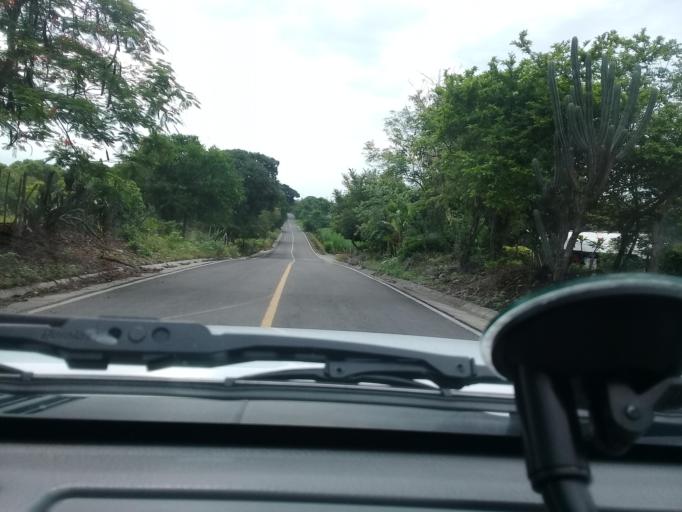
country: MX
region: Veracruz
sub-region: Paso de Ovejas
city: El Hatito
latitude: 19.3086
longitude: -96.4118
